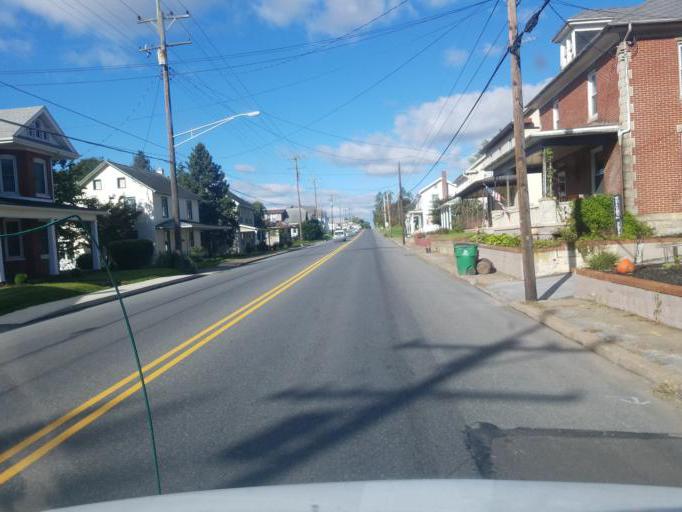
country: US
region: Pennsylvania
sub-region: Franklin County
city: Greencastle
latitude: 39.7790
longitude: -77.6745
